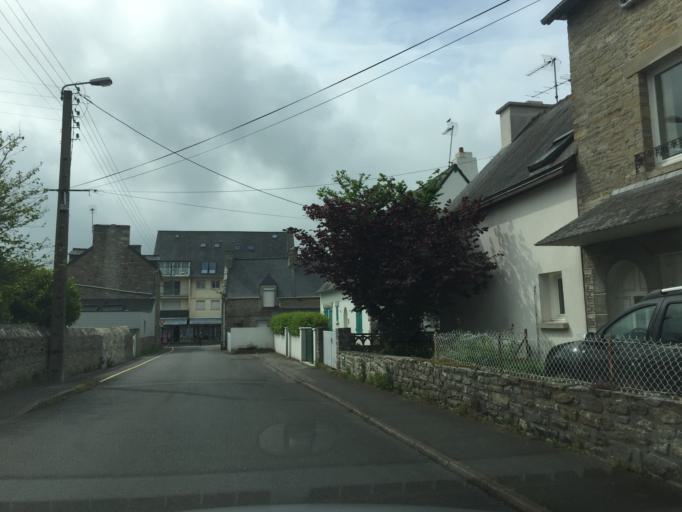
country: FR
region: Brittany
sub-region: Departement des Cotes-d'Armor
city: Saint-Cast-le-Guildo
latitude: 48.6382
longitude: -2.2585
